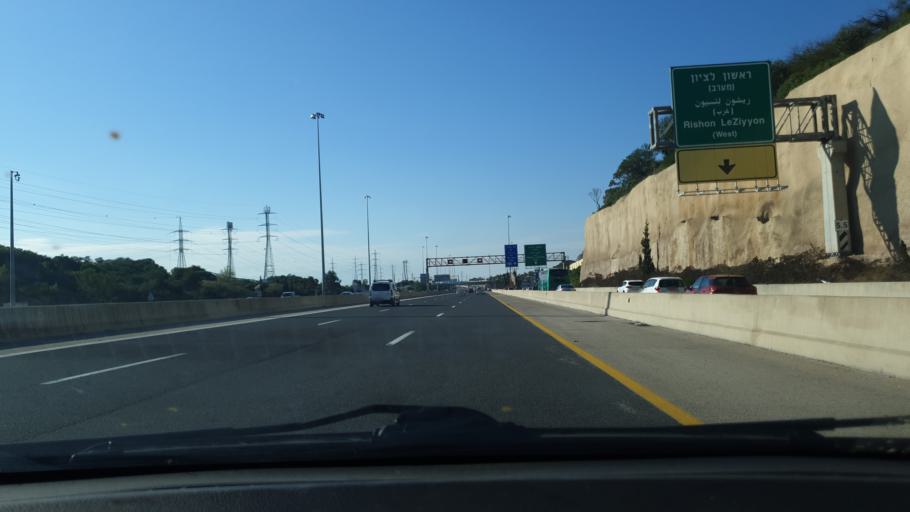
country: IL
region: Central District
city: Rishon LeZiyyon
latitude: 31.9591
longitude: 34.7740
